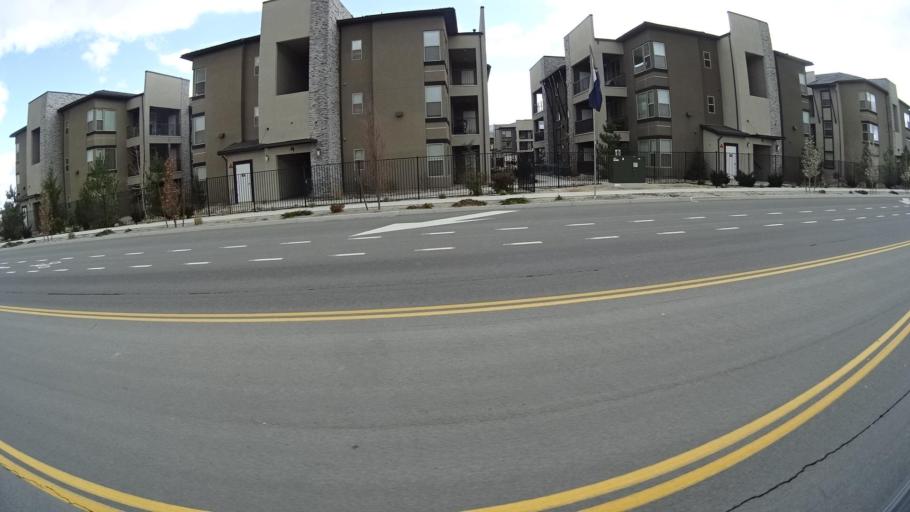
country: US
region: Nevada
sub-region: Washoe County
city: Sparks
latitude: 39.4137
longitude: -119.7596
